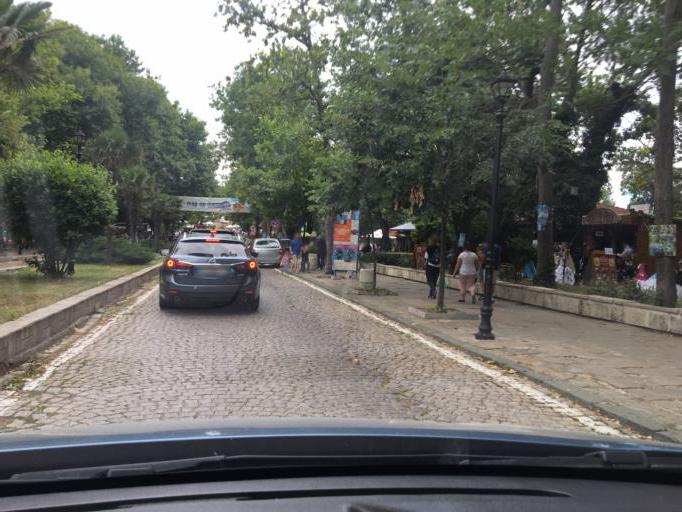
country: BG
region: Burgas
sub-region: Obshtina Sozopol
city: Sozopol
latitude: 42.4206
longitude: 27.6934
